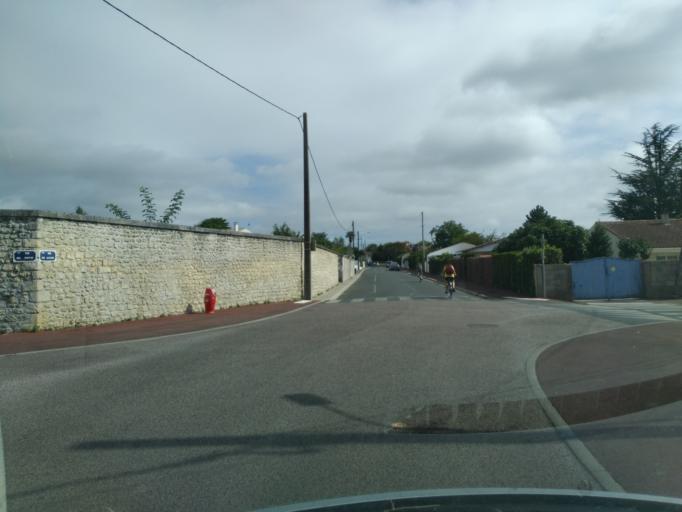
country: FR
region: Poitou-Charentes
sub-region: Departement de la Charente-Maritime
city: Saint-Palais-sur-Mer
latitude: 45.6509
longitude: -1.0767
